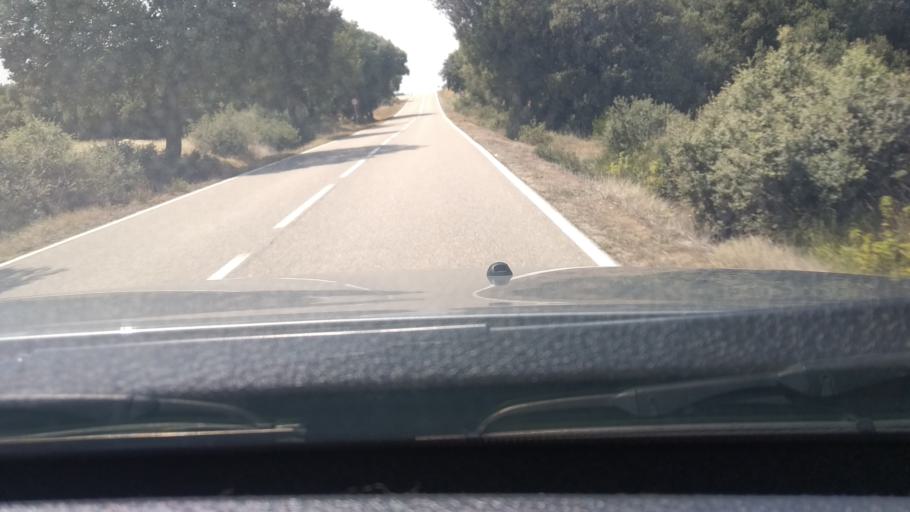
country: ES
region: Castille and Leon
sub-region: Provincia de Burgos
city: Avellanosa de Muno
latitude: 41.9774
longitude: -3.8000
